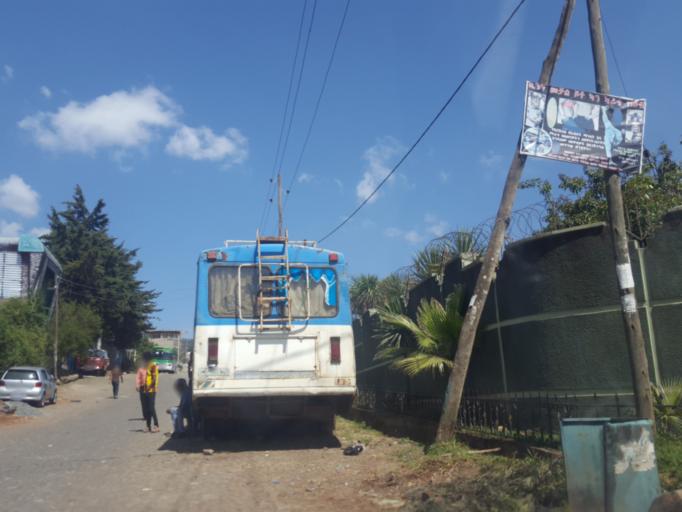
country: ET
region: Adis Abeba
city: Addis Ababa
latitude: 9.0605
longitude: 38.7334
